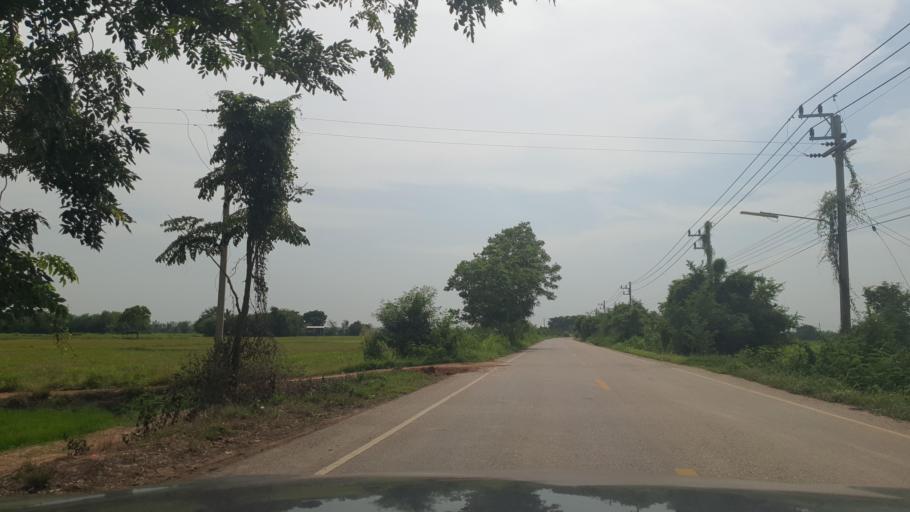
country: TH
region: Sukhothai
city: Si Samrong
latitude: 17.1161
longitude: 99.8821
